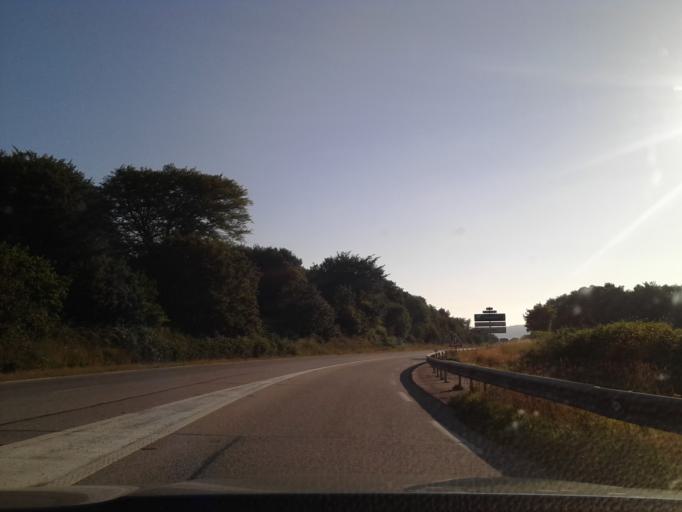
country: FR
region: Lower Normandy
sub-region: Departement de la Manche
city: La Glacerie
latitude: 49.6054
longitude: -1.5938
